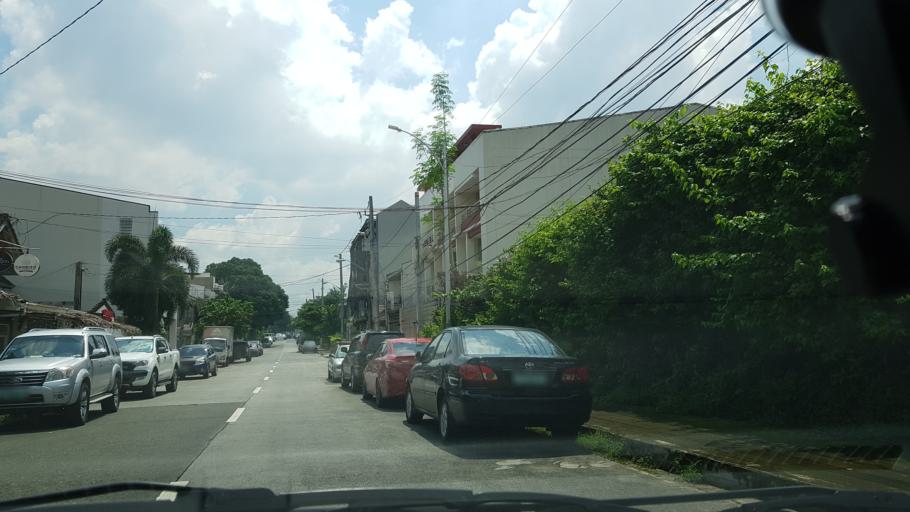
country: PH
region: Calabarzon
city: Del Monte
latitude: 14.6331
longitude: 121.0284
